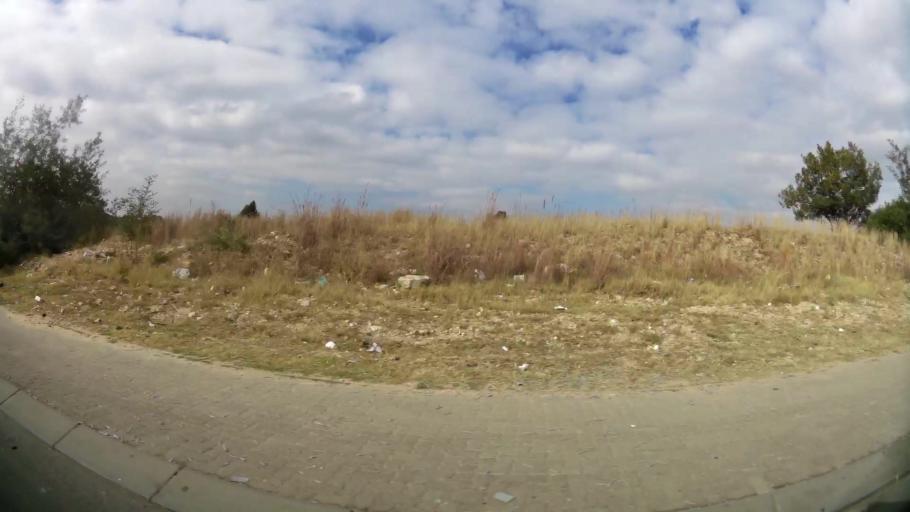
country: ZA
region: Gauteng
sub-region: City of Johannesburg Metropolitan Municipality
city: Roodepoort
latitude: -26.1933
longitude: 27.9039
